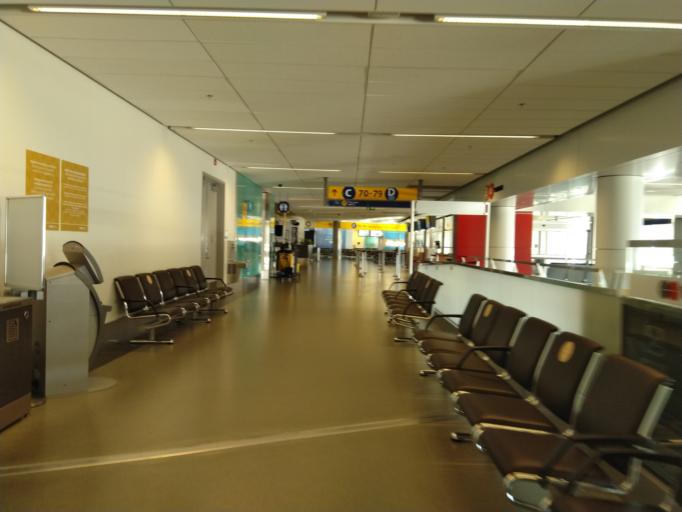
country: CA
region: Alberta
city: Calgary
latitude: 51.1302
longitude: -114.0064
